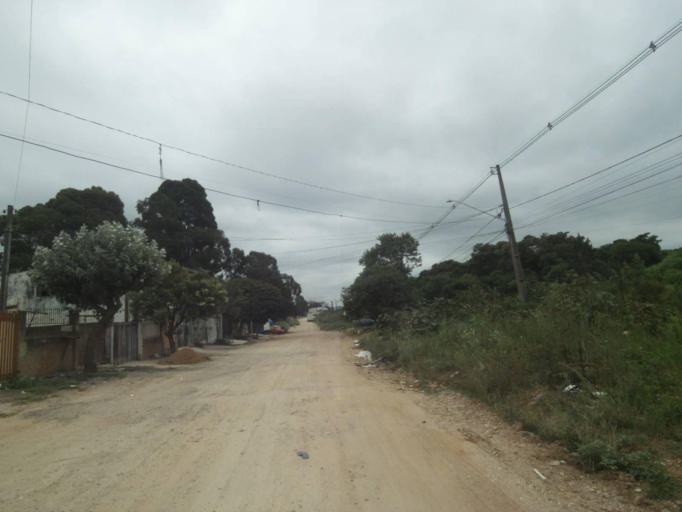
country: BR
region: Parana
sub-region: Araucaria
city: Araucaria
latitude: -25.5542
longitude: -49.3266
